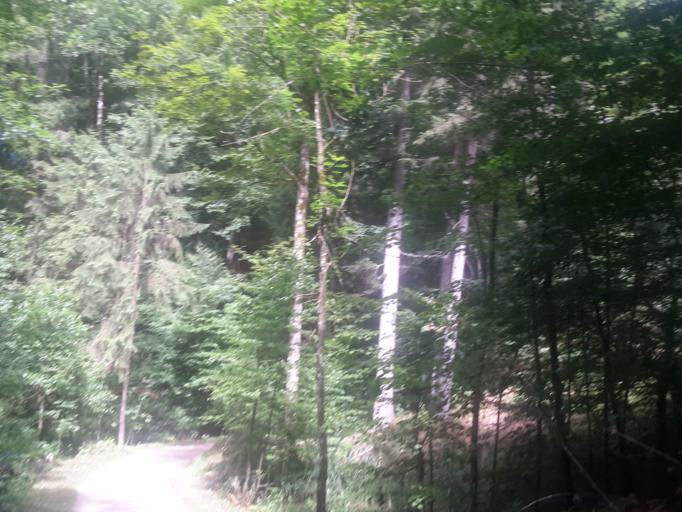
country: AT
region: Tyrol
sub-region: Politischer Bezirk Kufstein
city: Kufstein
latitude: 47.6008
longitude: 12.1528
